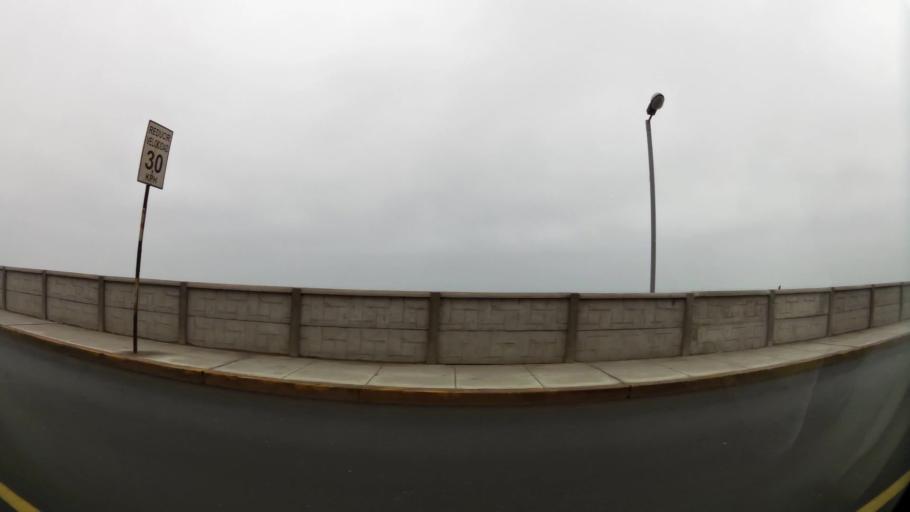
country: PE
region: Callao
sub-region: Callao
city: Callao
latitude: -12.0753
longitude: -77.1197
